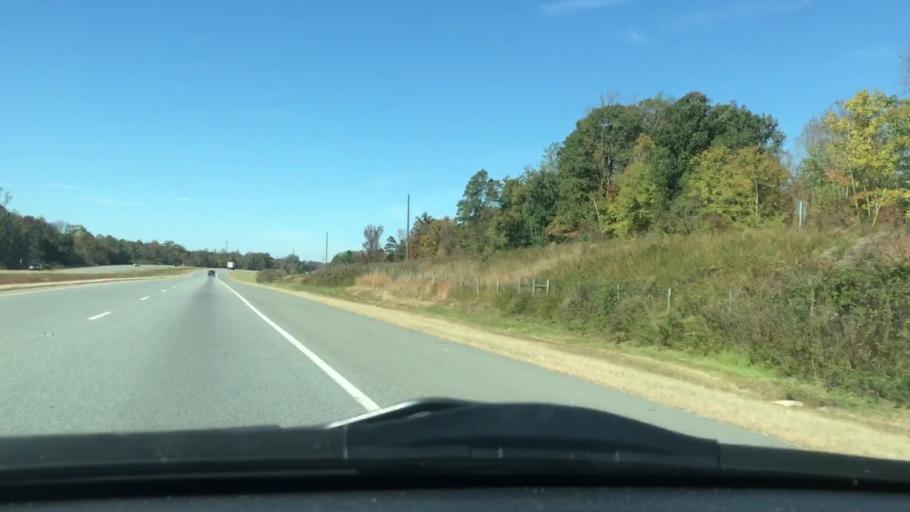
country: US
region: North Carolina
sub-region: Randolph County
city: Archdale
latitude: 35.8773
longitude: -79.9062
